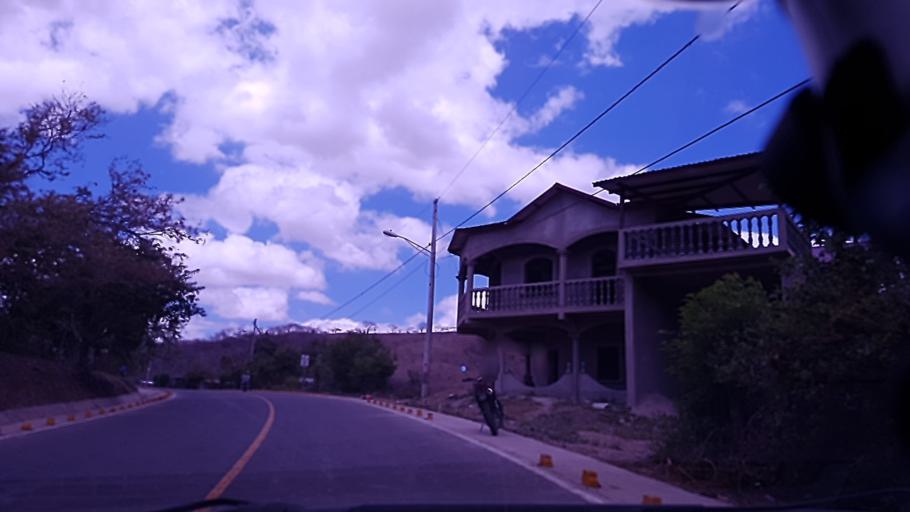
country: NI
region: Esteli
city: Condega
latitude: 13.3770
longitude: -86.3883
